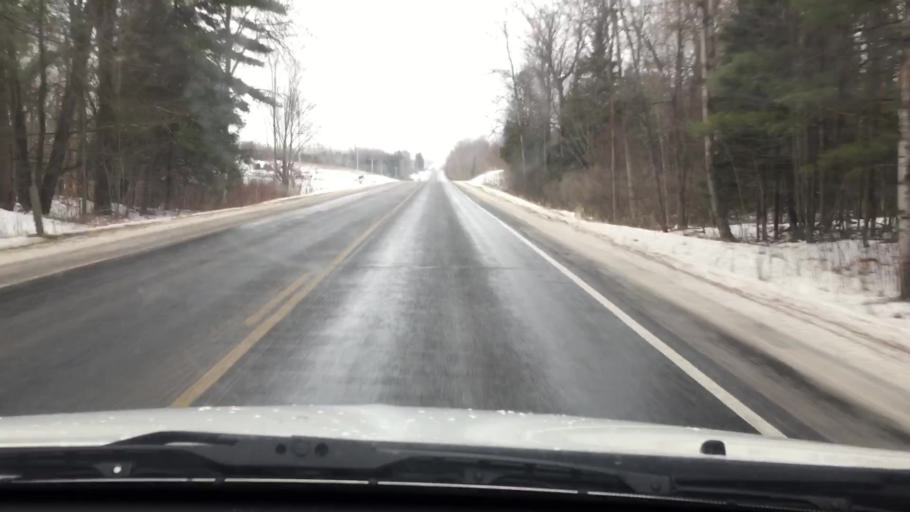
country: US
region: Michigan
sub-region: Osceola County
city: Reed City
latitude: 44.0534
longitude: -85.4439
